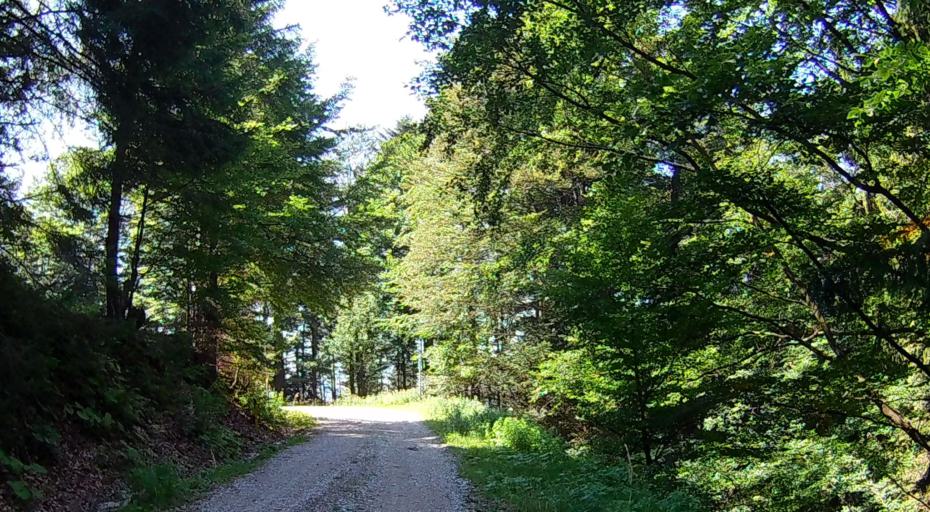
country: SI
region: Selnica ob Dravi
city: Selnica ob Dravi
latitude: 46.4895
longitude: 15.4590
